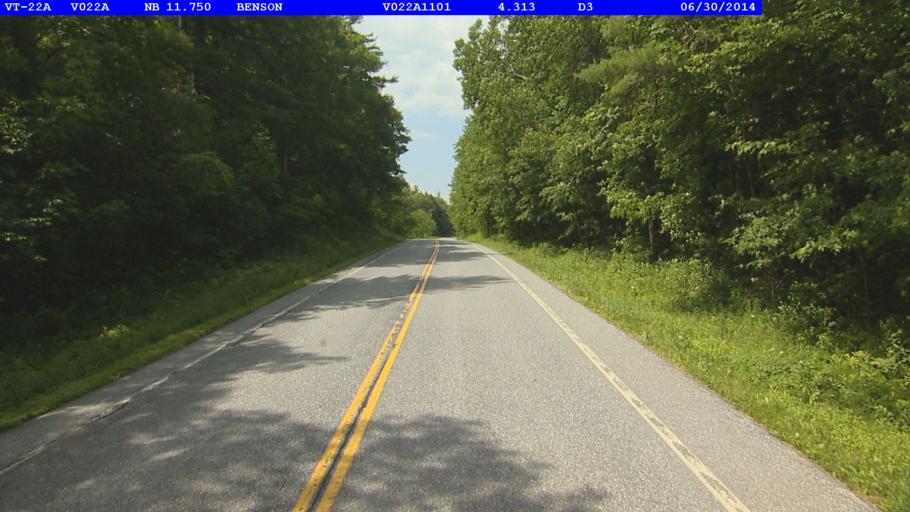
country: US
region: Vermont
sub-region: Rutland County
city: Fair Haven
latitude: 43.7301
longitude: -73.3030
